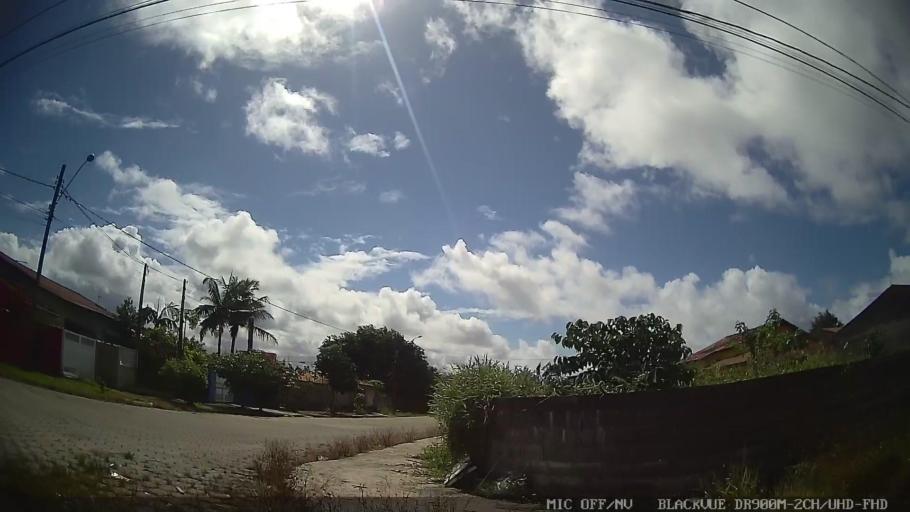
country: BR
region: Sao Paulo
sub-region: Itanhaem
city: Itanhaem
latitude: -24.2218
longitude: -46.8606
